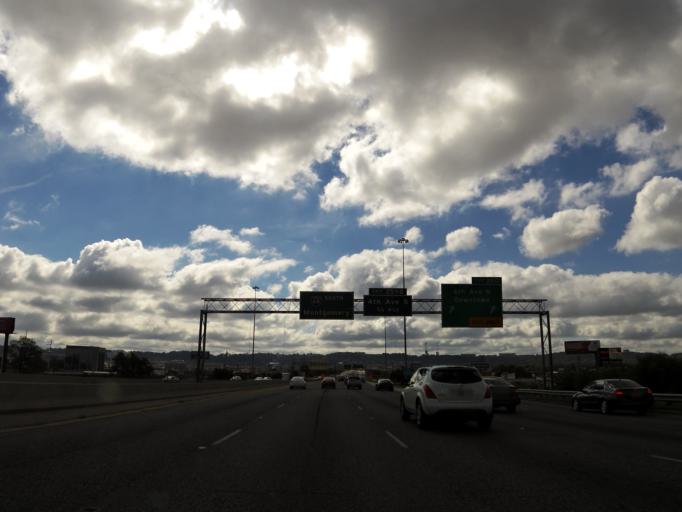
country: US
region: Alabama
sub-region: Jefferson County
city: Birmingham
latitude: 33.5151
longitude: -86.8238
